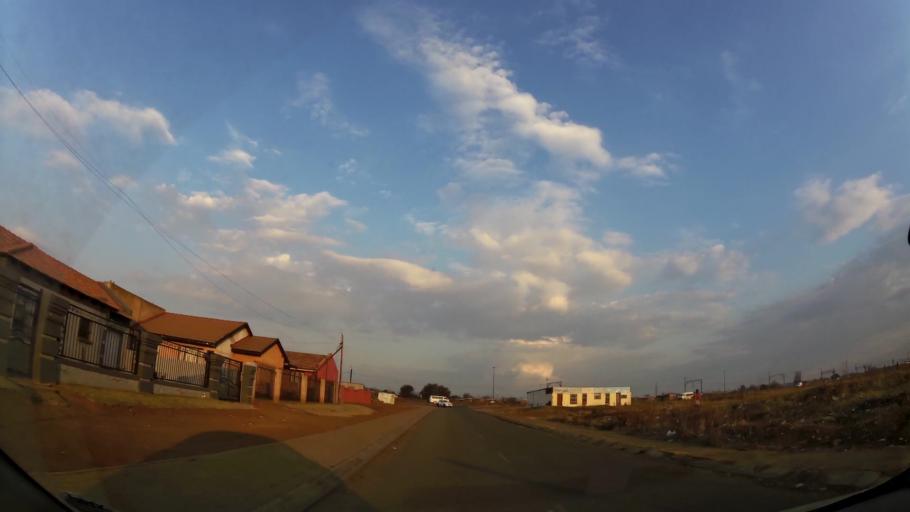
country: ZA
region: Gauteng
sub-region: City of Johannesburg Metropolitan Municipality
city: Orange Farm
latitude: -26.5500
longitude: 27.8828
